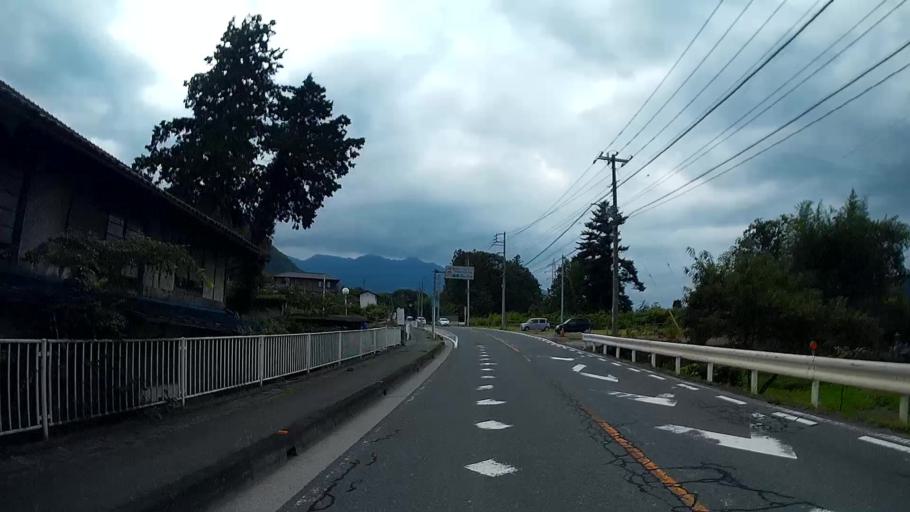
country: JP
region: Saitama
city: Chichibu
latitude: 35.9647
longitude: 139.0551
